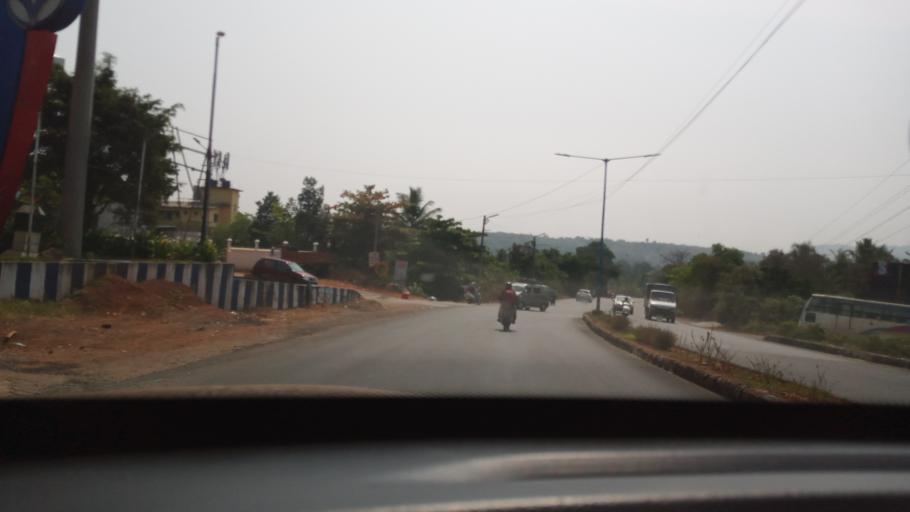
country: IN
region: Goa
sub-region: South Goa
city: Sancoale
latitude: 15.3612
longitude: 73.9273
